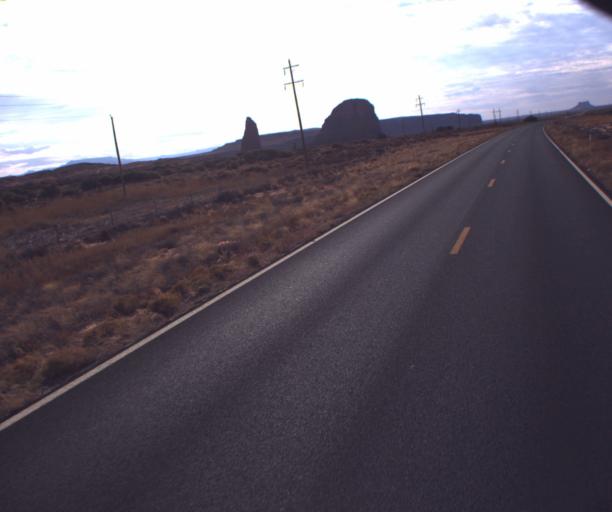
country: US
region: Arizona
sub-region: Apache County
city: Many Farms
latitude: 36.6795
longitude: -109.6025
